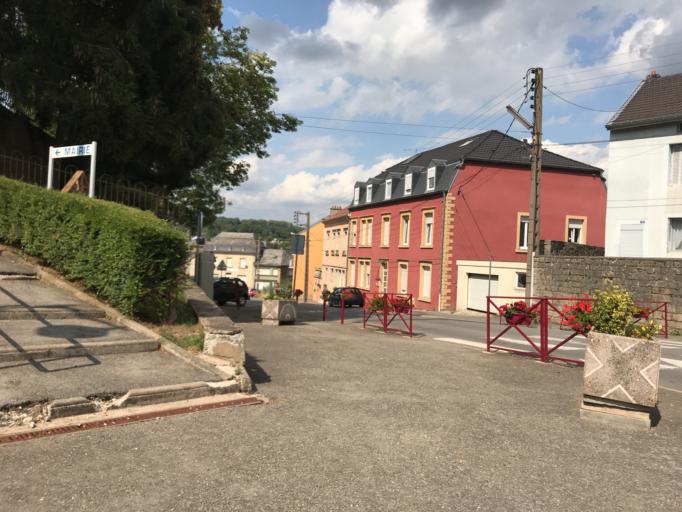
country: FR
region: Lorraine
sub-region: Departement de Meurthe-et-Moselle
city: Thil
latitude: 49.4931
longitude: 5.9193
